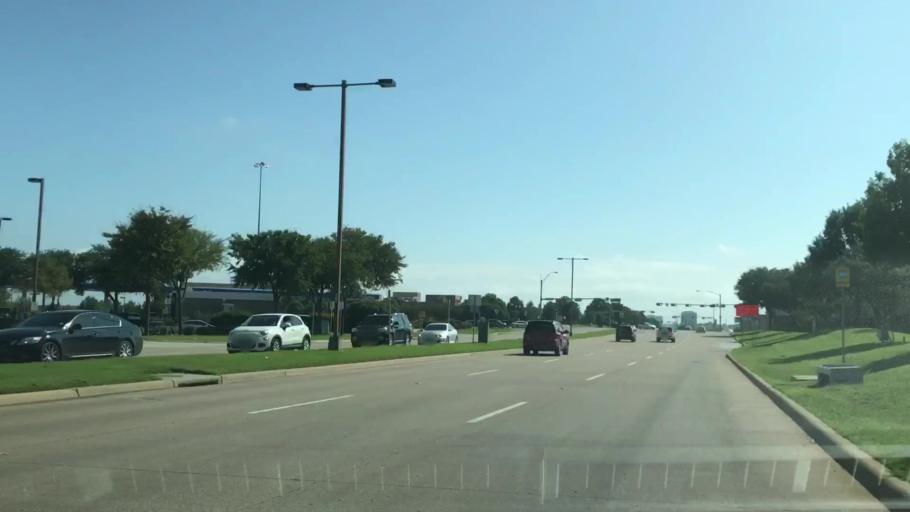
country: US
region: Texas
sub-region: Dallas County
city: Farmers Branch
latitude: 32.9068
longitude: -96.9589
